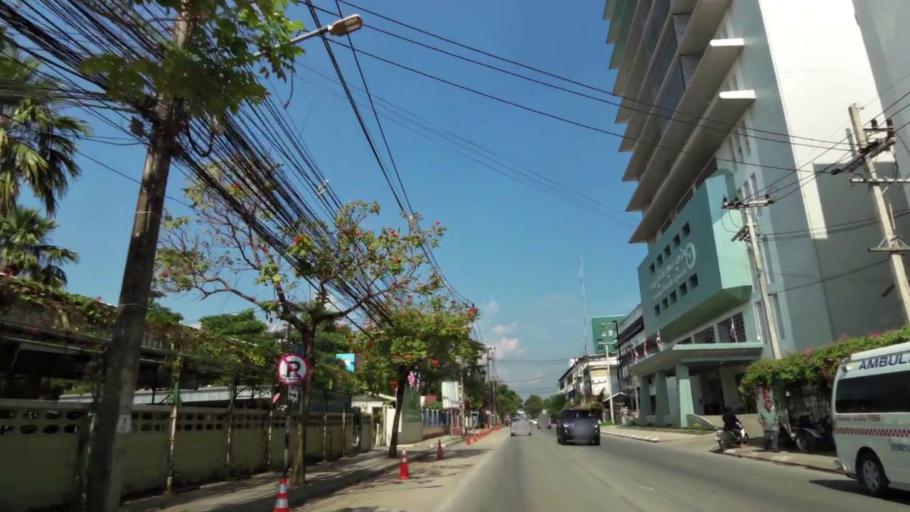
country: TH
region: Chiang Rai
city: Chiang Rai
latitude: 19.9003
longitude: 99.8280
